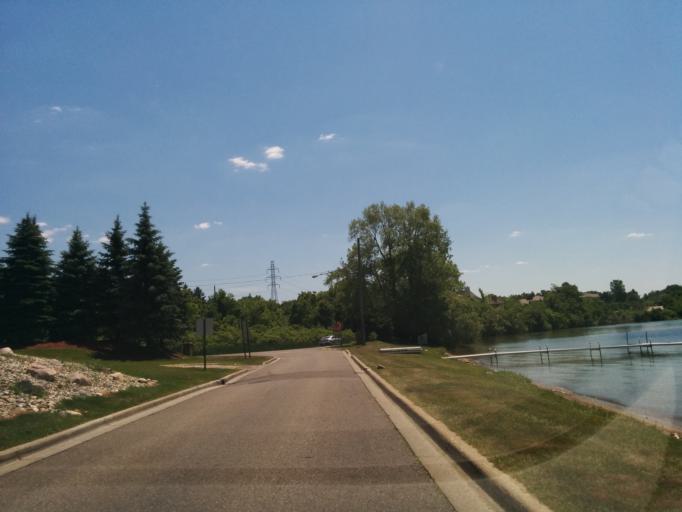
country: US
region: Michigan
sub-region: Oakland County
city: Orchard Lake
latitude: 42.5869
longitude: -83.3564
